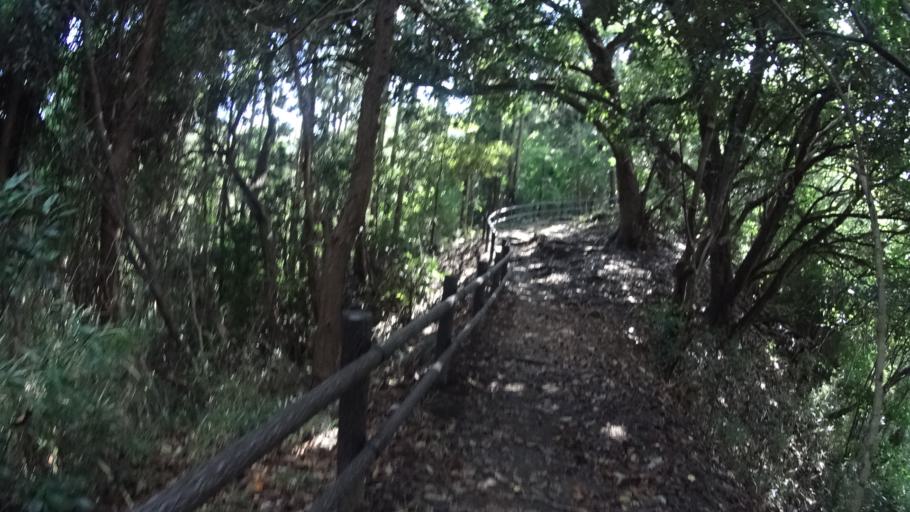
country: JP
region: Kanagawa
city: Kamakura
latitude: 35.3583
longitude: 139.5859
